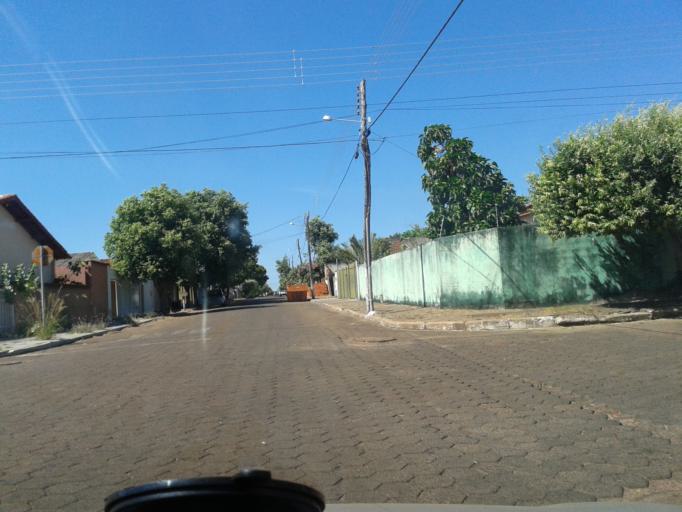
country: BR
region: Goias
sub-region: Sao Miguel Do Araguaia
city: Sao Miguel do Araguaia
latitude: -13.2740
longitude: -50.1605
